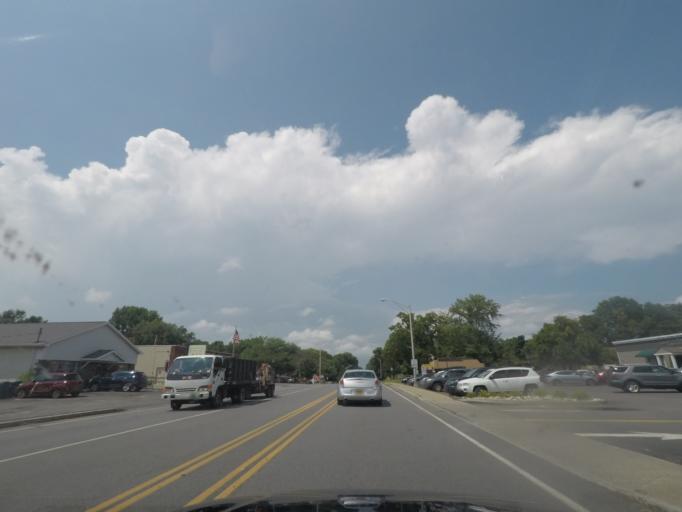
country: US
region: New York
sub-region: Albany County
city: West Albany
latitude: 42.7070
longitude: -73.7774
